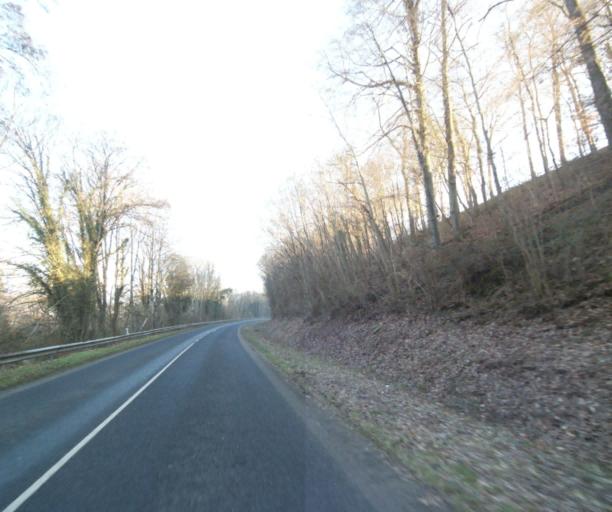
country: FR
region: Champagne-Ardenne
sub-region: Departement de la Haute-Marne
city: Bienville
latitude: 48.5583
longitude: 5.0602
